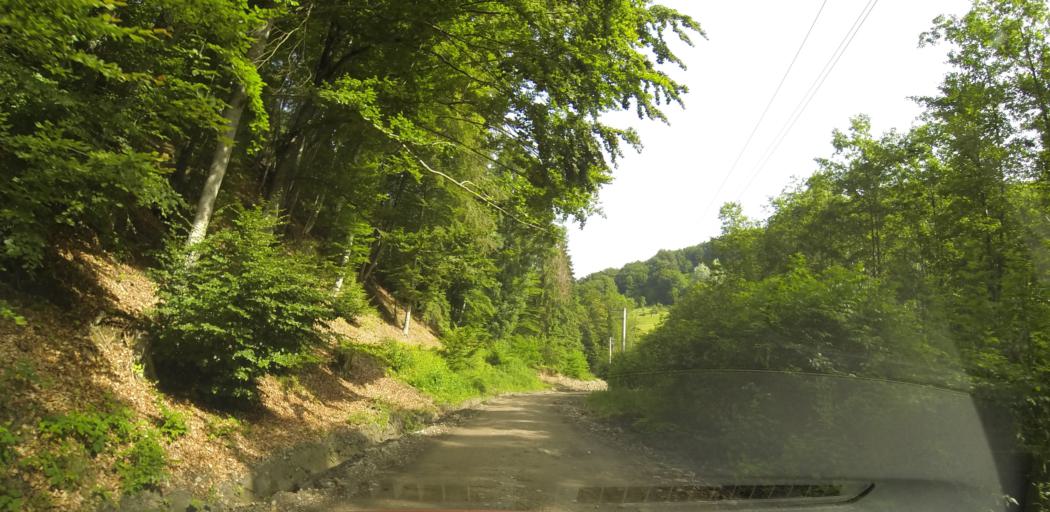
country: RO
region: Valcea
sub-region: Oras Baile Olanesti
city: Baile Olanesti
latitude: 45.2196
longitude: 24.2155
